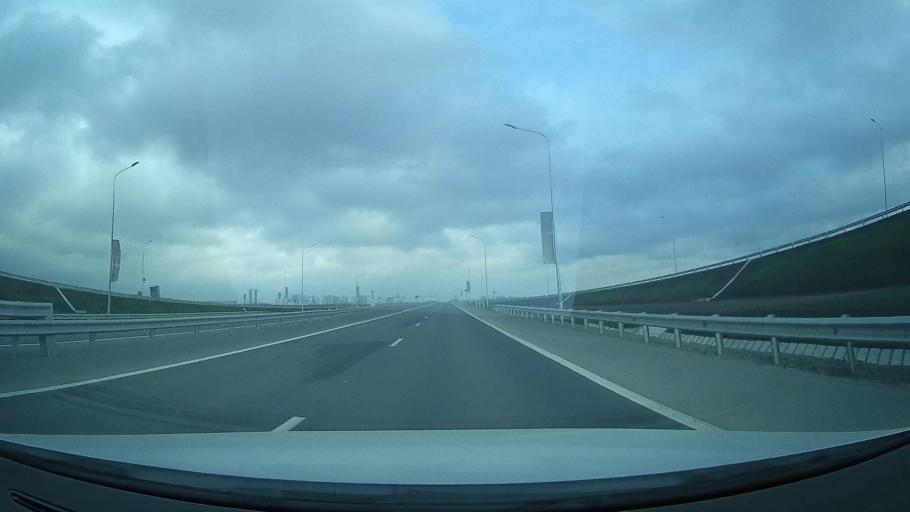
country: RU
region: Rostov
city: Grushevskaya
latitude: 47.4867
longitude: 39.9365
